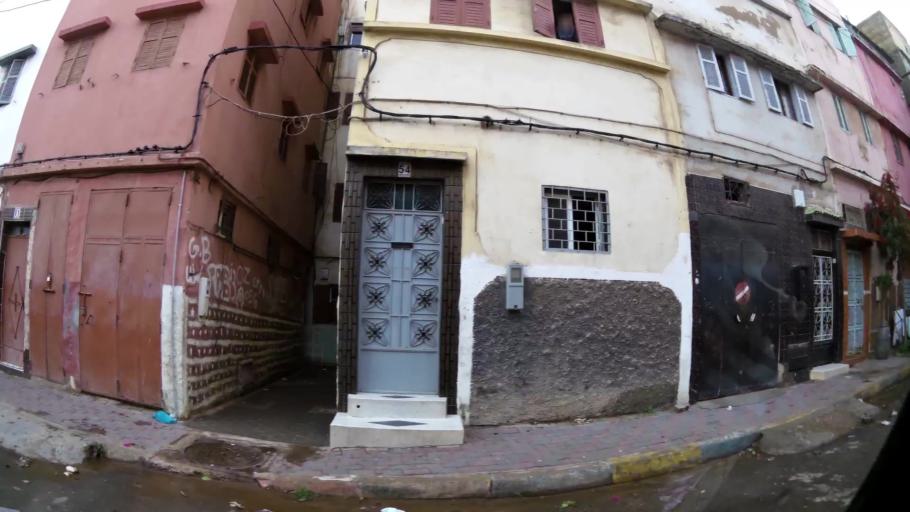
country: MA
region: Grand Casablanca
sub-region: Casablanca
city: Casablanca
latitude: 33.5489
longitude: -7.5754
